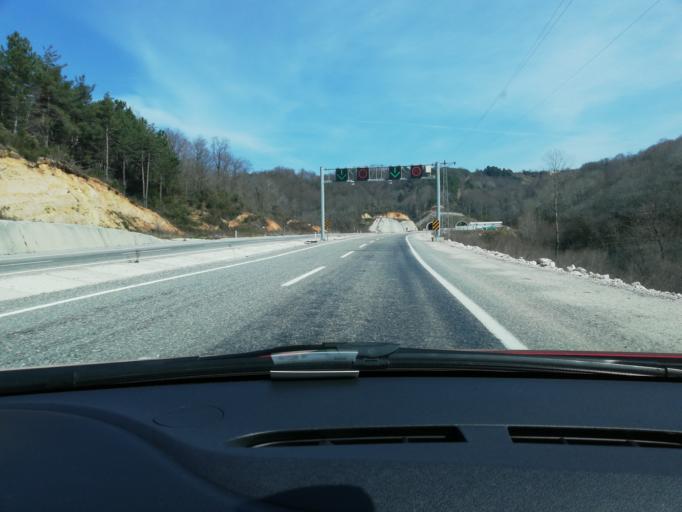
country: TR
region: Bartin
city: Amasra
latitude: 41.7733
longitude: 32.5051
